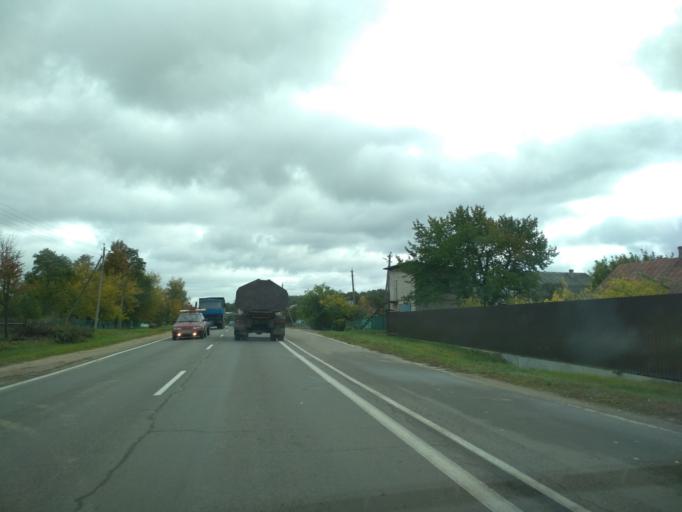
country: BY
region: Minsk
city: Mar''ina Horka
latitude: 53.5246
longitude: 28.1437
